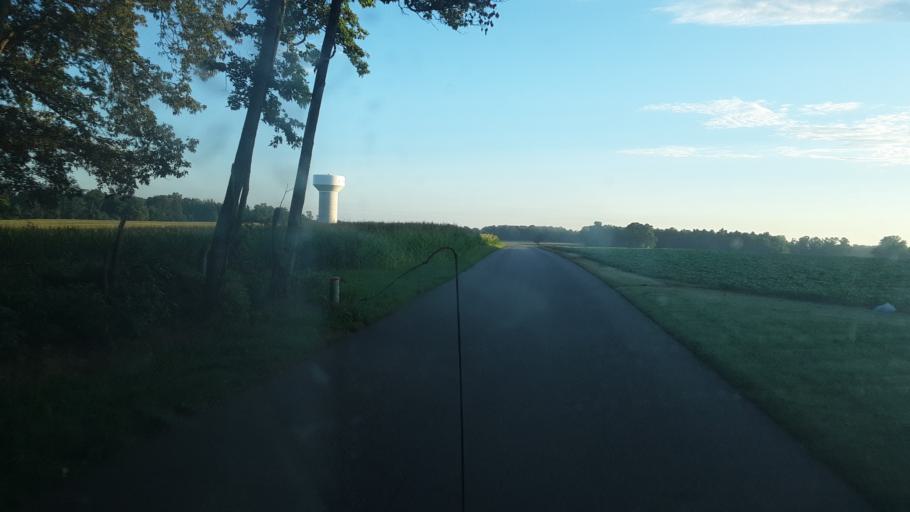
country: US
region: Kentucky
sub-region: Todd County
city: Guthrie
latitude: 36.7005
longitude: -87.1701
